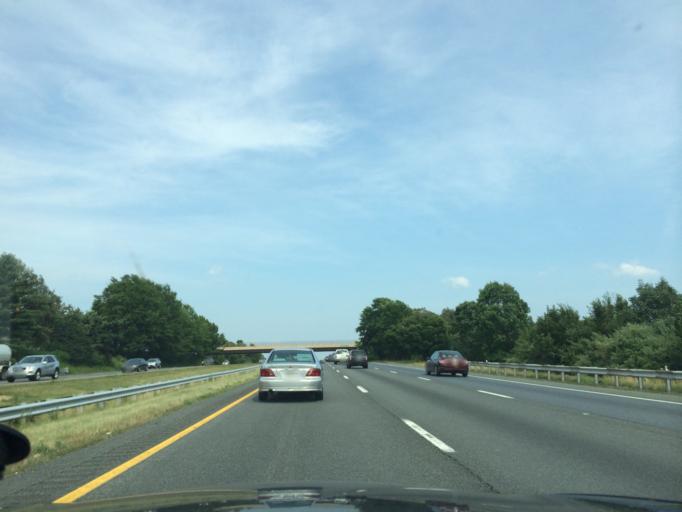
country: US
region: Maryland
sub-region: Frederick County
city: Spring Ridge
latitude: 39.3864
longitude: -77.3011
